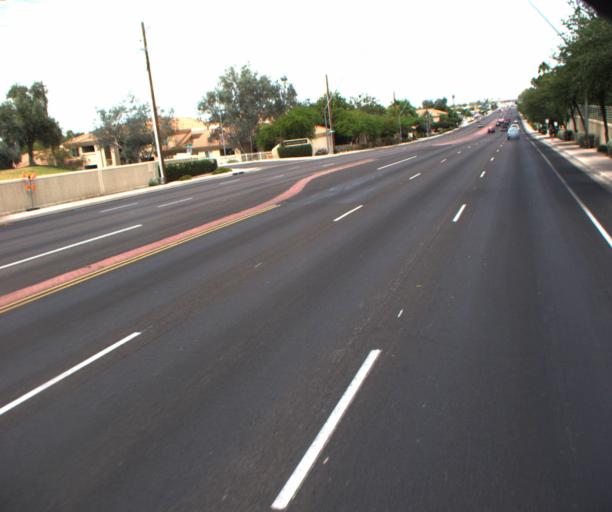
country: US
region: Arizona
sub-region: Maricopa County
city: Mesa
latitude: 33.4396
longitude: -111.8398
